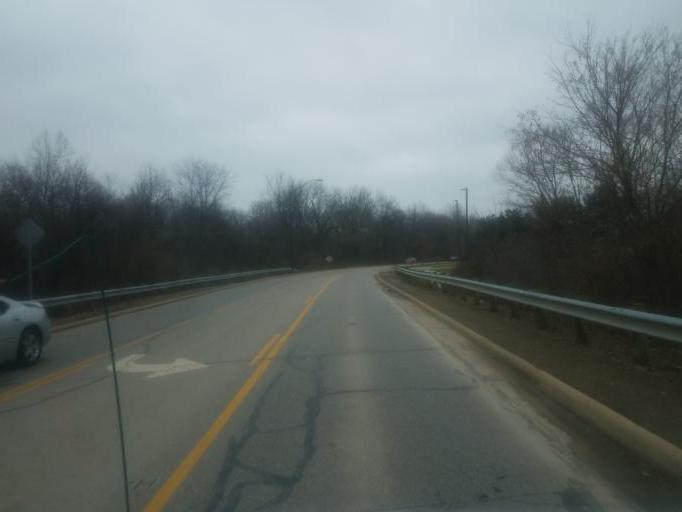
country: US
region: Ohio
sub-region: Franklin County
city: Westerville
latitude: 40.1170
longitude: -82.9403
